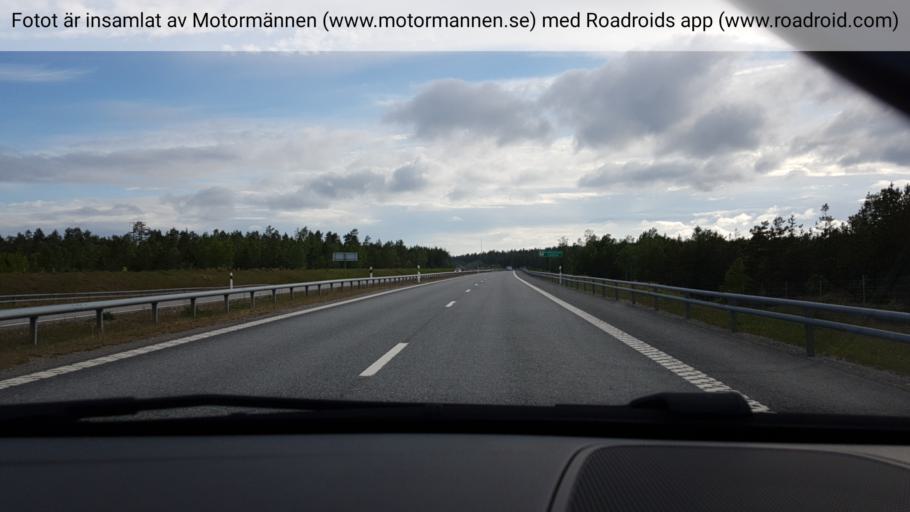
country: SE
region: Stockholm
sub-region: Nynashamns Kommun
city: Osmo
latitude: 59.0486
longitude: 17.9892
